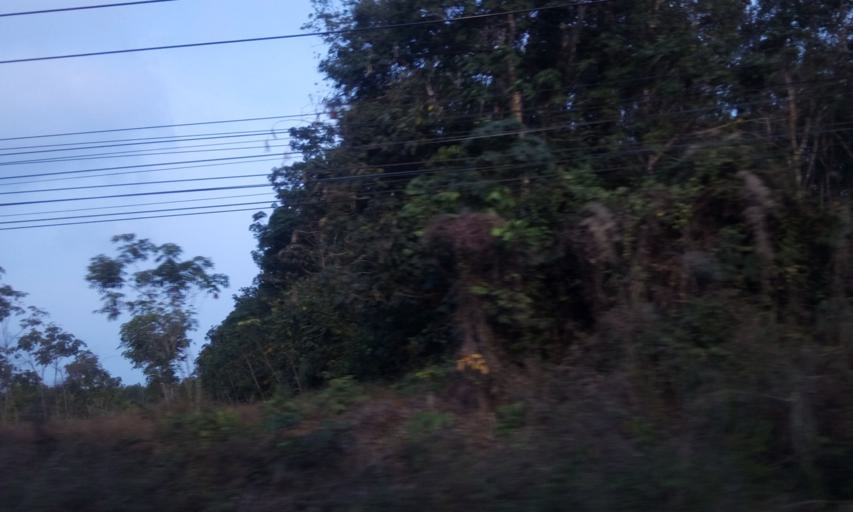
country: TH
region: Trat
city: Khao Saming
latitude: 12.3349
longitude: 102.3700
